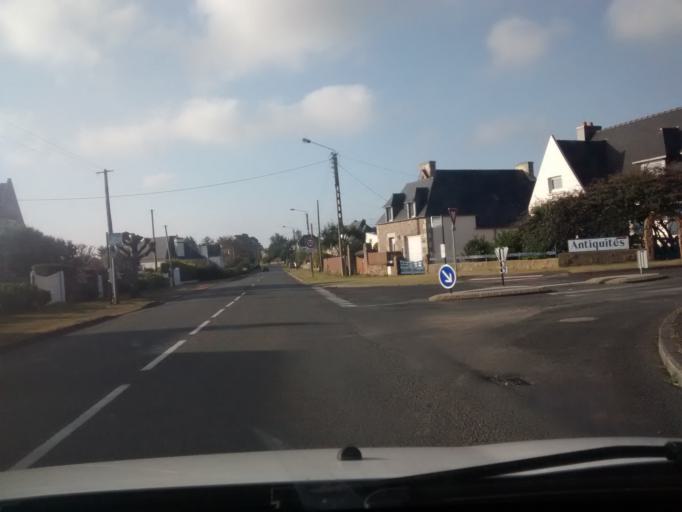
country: FR
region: Brittany
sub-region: Departement des Cotes-d'Armor
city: Tregastel
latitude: 48.8179
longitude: -3.4698
